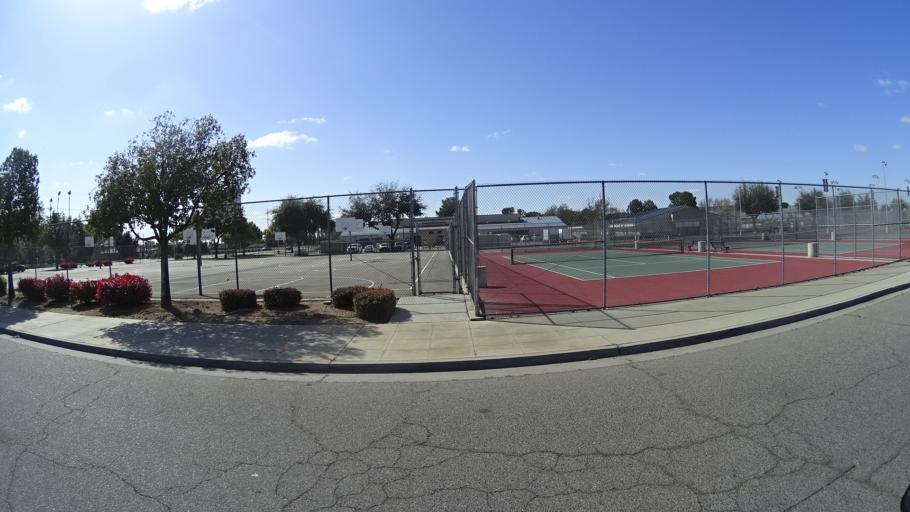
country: US
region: California
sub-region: Fresno County
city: West Park
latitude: 36.7899
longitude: -119.8811
